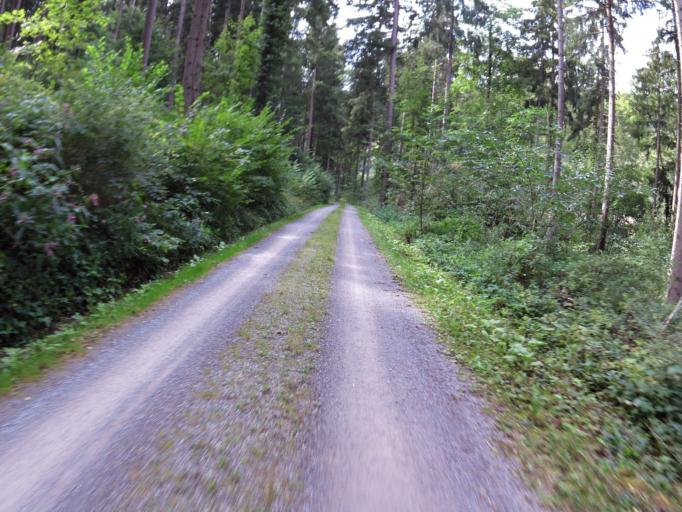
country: DE
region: Baden-Wuerttemberg
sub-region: Freiburg Region
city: Sulz am Neckar
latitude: 48.3512
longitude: 8.5985
